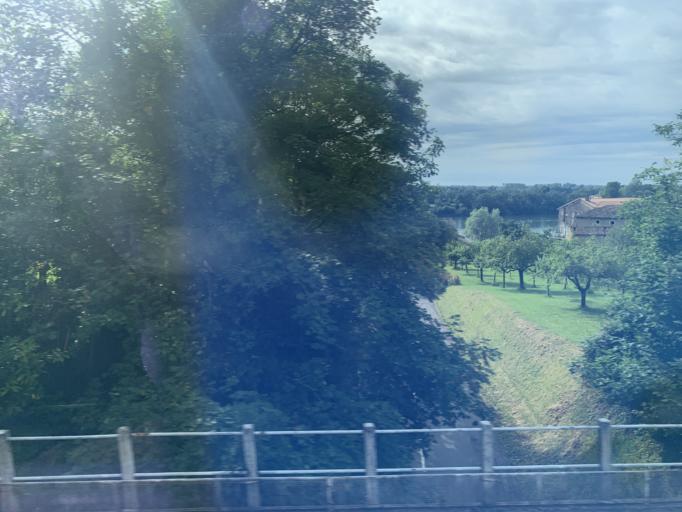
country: FR
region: Bourgogne
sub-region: Departement de Saone-et-Loire
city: Saint-Martin-Belle-Roche
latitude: 46.3622
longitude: 4.8520
